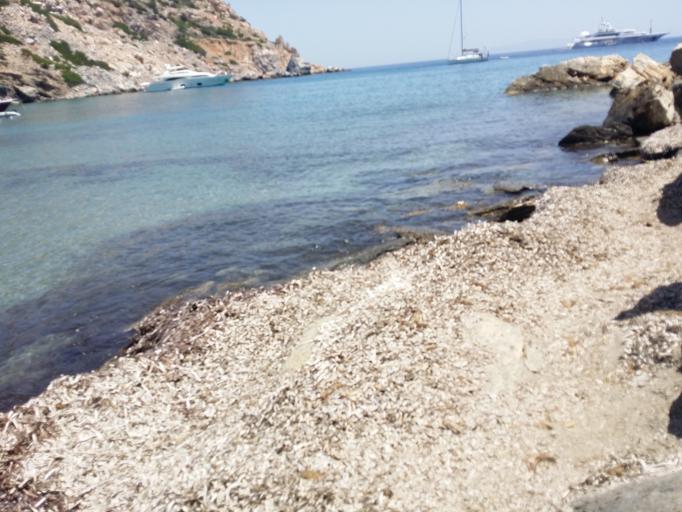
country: GR
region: South Aegean
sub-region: Nomos Kykladon
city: Antiparos
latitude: 36.9548
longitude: 24.9993
